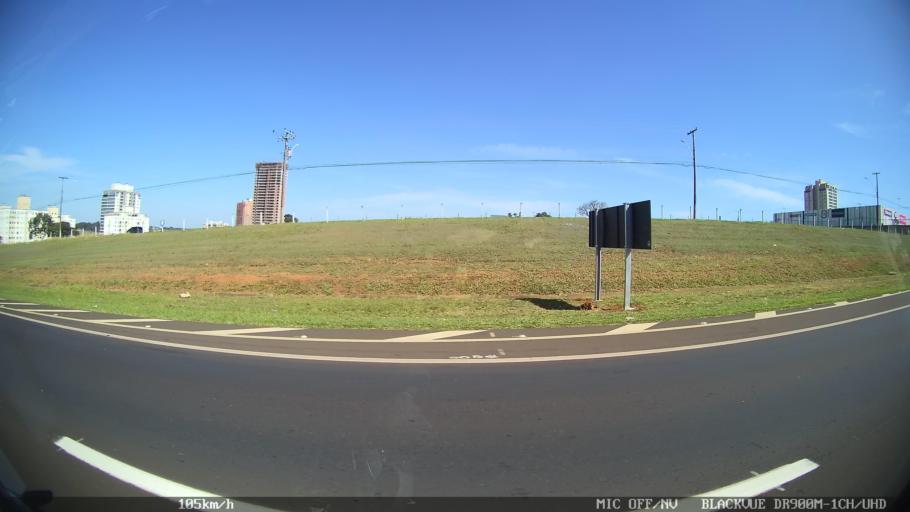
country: BR
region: Sao Paulo
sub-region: Franca
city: Franca
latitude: -20.5488
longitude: -47.4140
